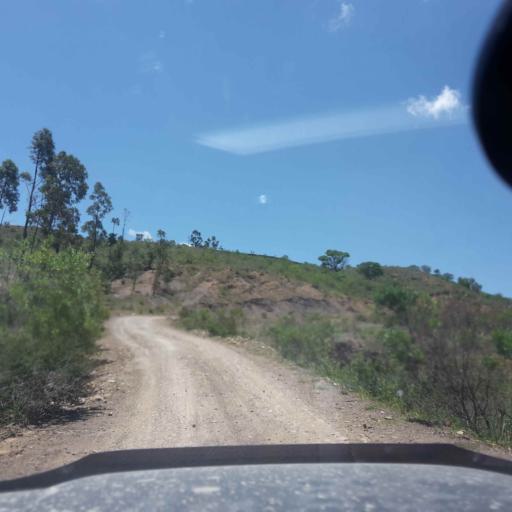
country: BO
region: Cochabamba
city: Totora
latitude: -17.7690
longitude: -65.2616
